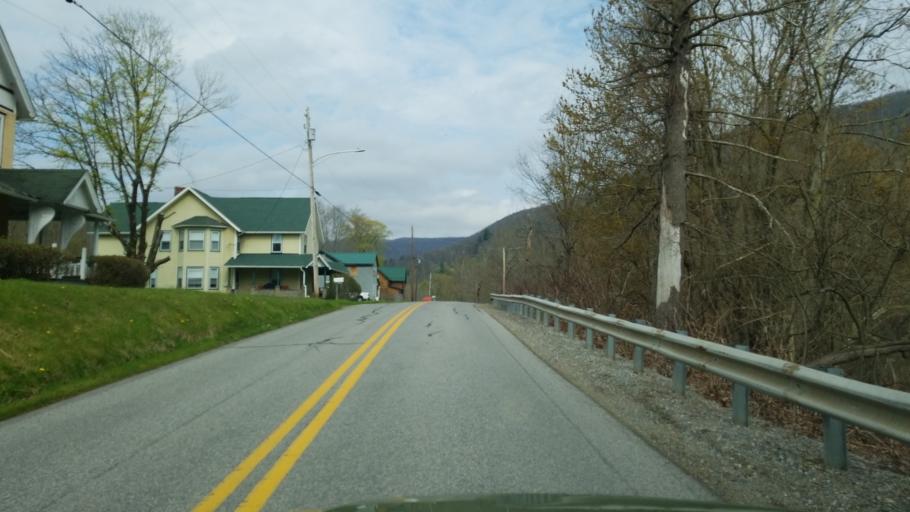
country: US
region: Pennsylvania
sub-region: Cameron County
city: Emporium
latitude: 41.3164
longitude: -78.0809
